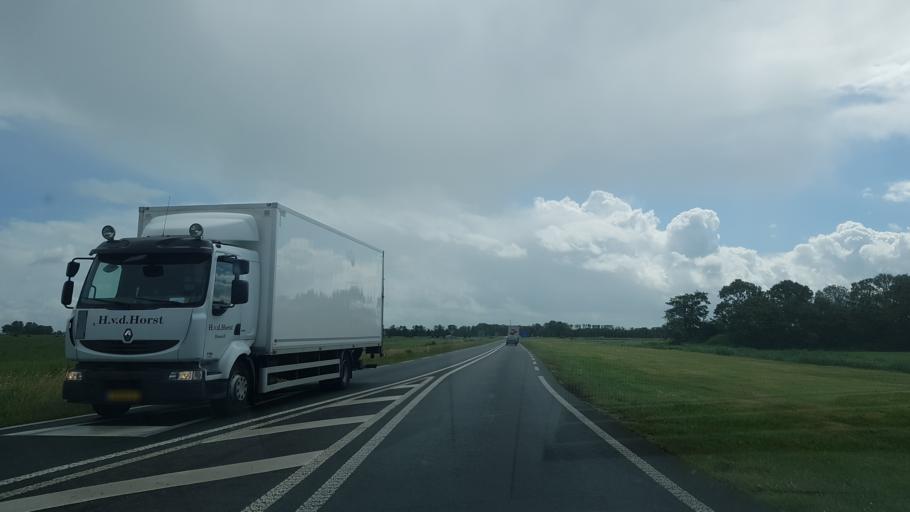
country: NL
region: Friesland
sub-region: Gemeente Dongeradeel
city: Dokkum
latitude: 53.3115
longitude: 6.0118
